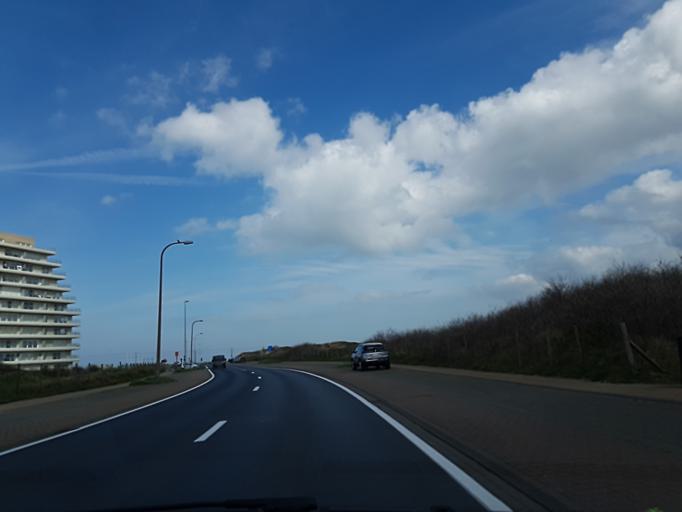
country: BE
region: Flanders
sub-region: Provincie West-Vlaanderen
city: Middelkerke
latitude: 51.1902
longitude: 2.8239
